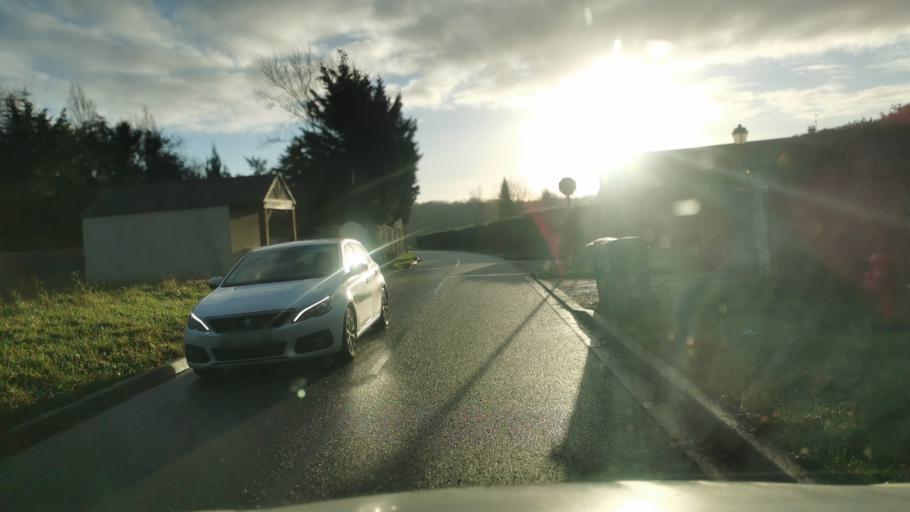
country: FR
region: Ile-de-France
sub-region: Departement des Yvelines
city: Houdan
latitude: 48.8345
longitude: 1.6139
